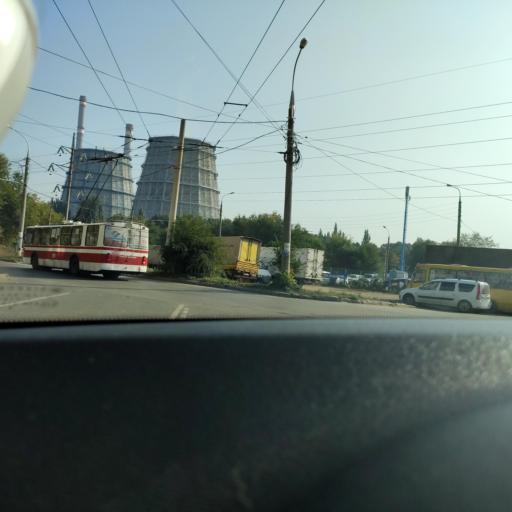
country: RU
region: Samara
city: Petra-Dubrava
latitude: 53.2499
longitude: 50.2651
